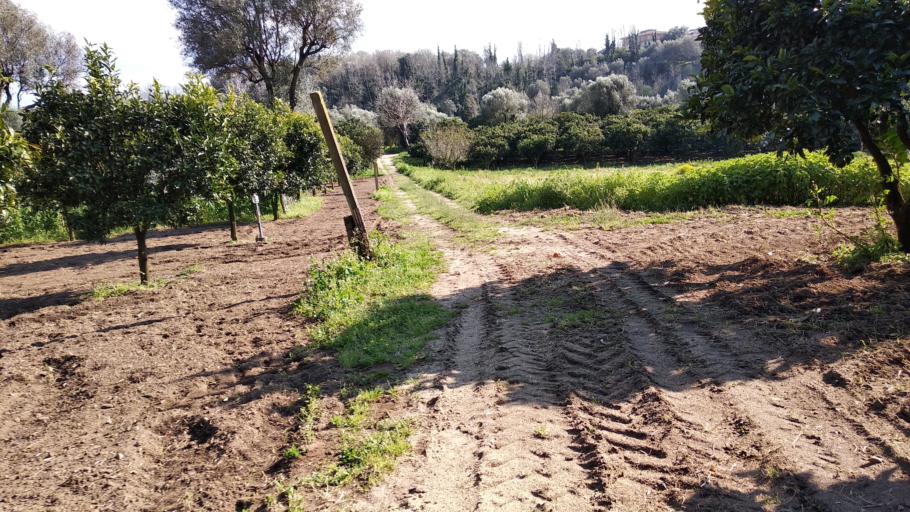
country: IT
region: Calabria
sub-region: Provincia di Reggio Calabria
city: Rizziconi
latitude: 38.4312
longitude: 15.9595
